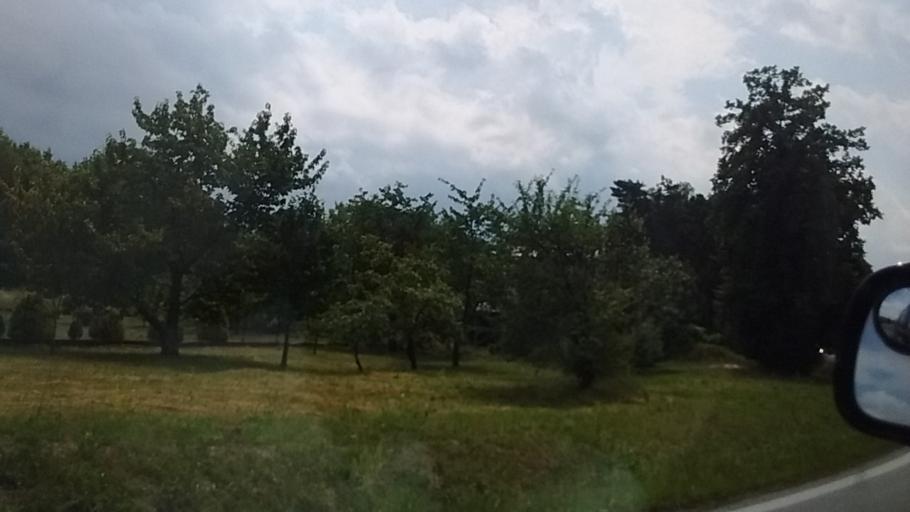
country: PL
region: Subcarpathian Voivodeship
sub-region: Powiat lancucki
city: Zolynia
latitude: 50.1887
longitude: 22.3226
